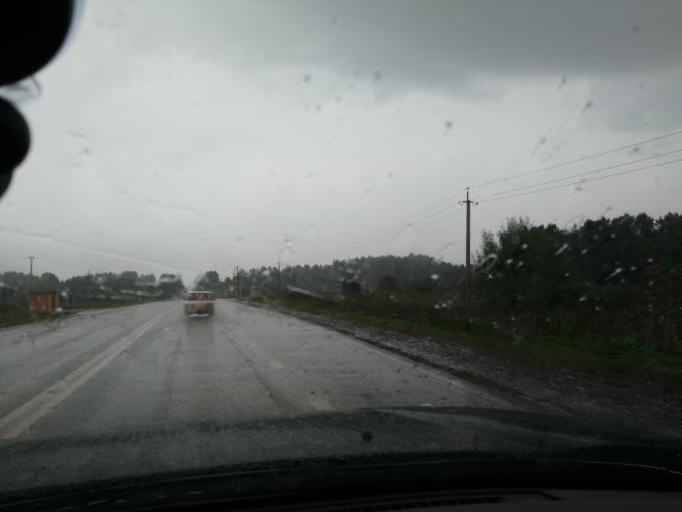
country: RU
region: Perm
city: Osa
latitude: 57.1558
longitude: 55.5299
